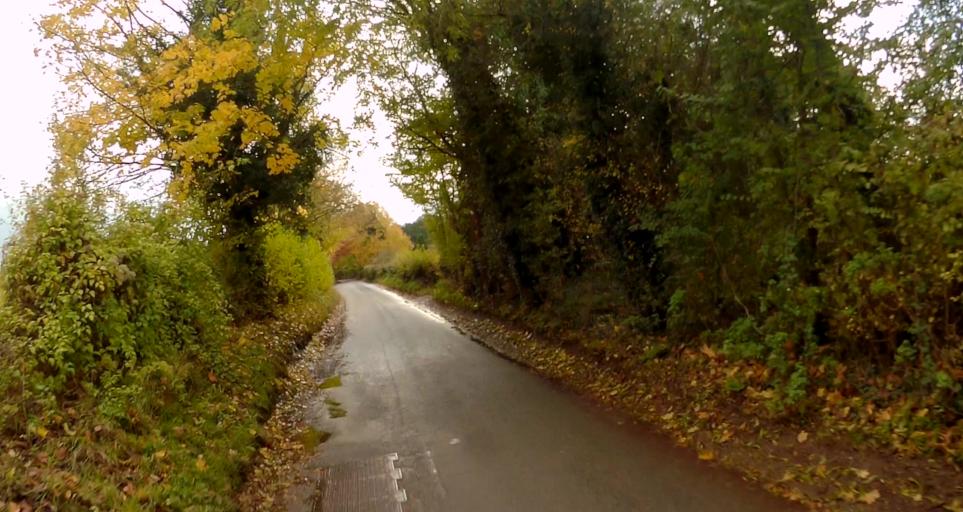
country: GB
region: England
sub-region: Hampshire
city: Old Basing
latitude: 51.2342
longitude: -1.0292
